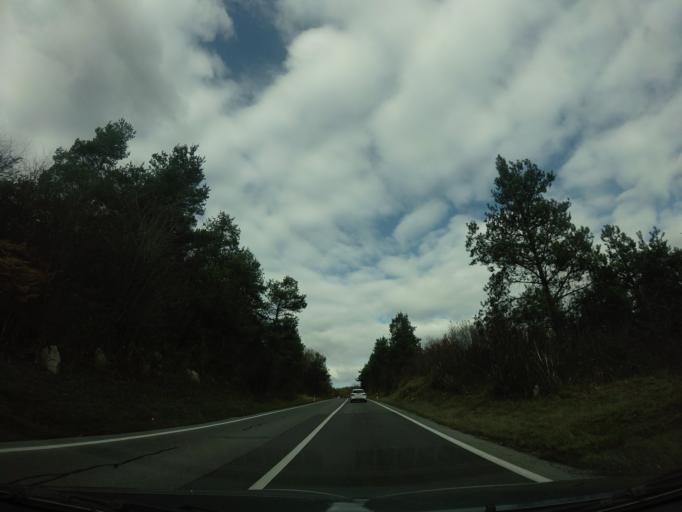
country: HR
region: Karlovacka
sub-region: Grad Karlovac
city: Slunj
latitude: 45.0371
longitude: 15.6358
